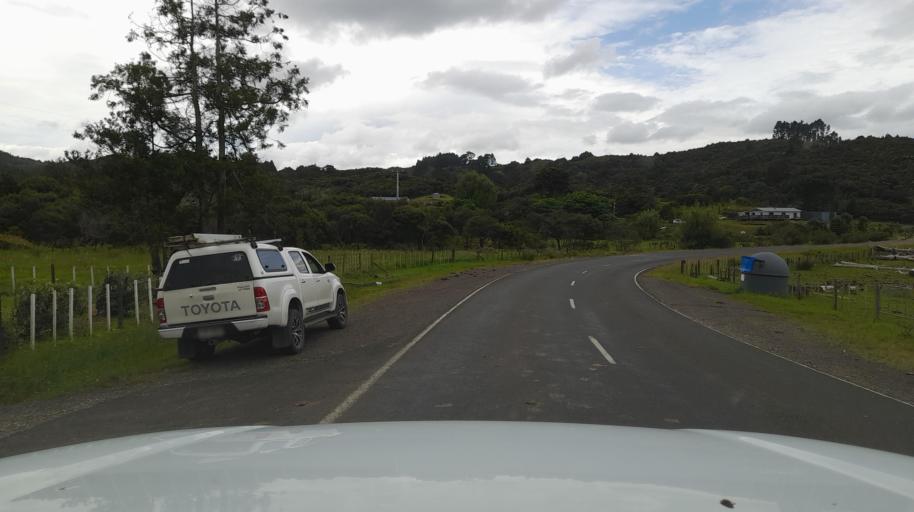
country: NZ
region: Northland
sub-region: Far North District
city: Kaitaia
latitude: -35.3678
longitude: 173.3817
